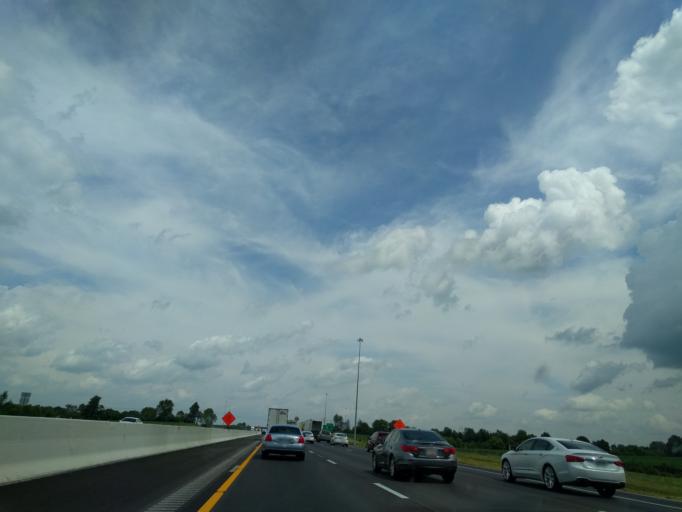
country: US
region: Kentucky
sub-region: Larue County
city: Hodgenville
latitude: 37.5145
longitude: -85.8864
